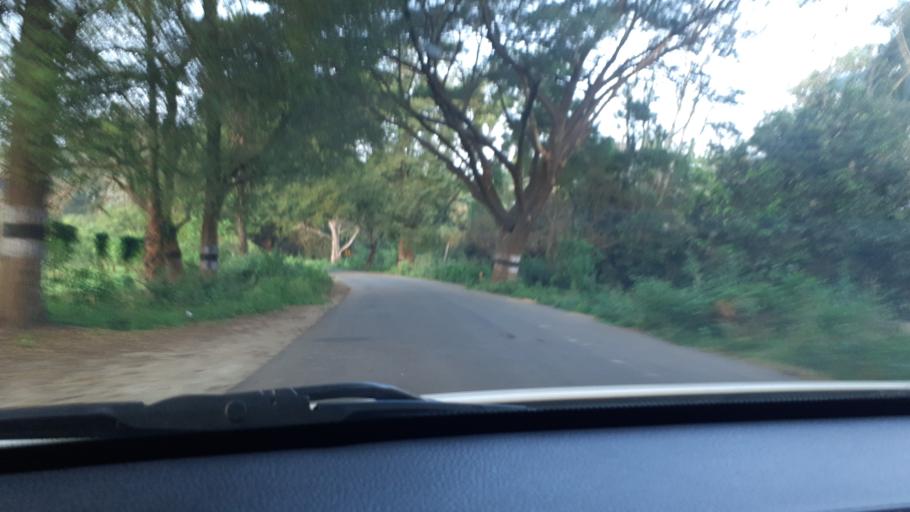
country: IN
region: Tamil Nadu
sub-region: Dindigul
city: Ayakudi
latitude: 10.4005
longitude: 77.5444
